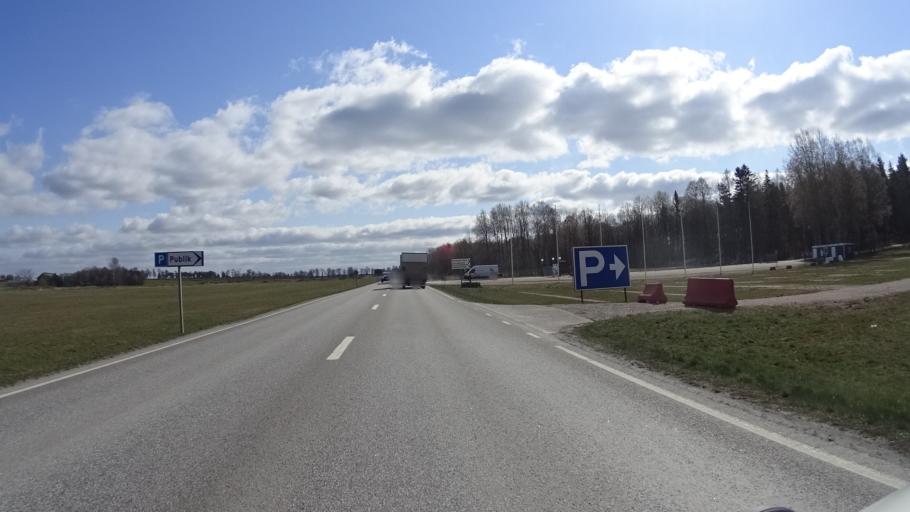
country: SE
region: OEstergoetland
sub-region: Mjolby Kommun
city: Mantorp
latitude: 58.3753
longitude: 15.2822
